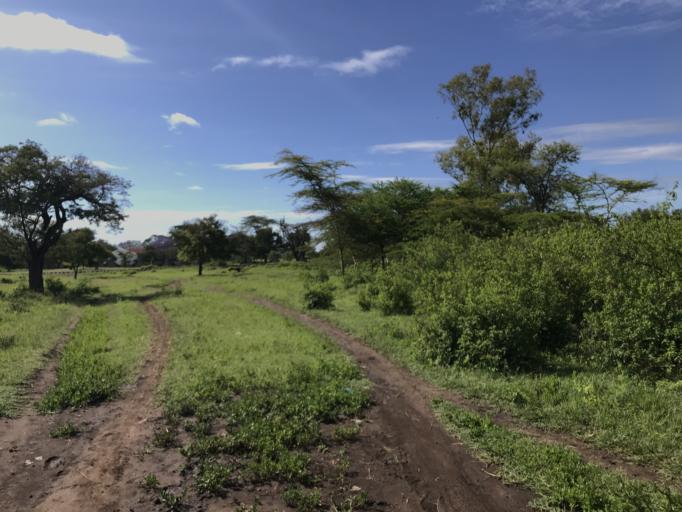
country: TZ
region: Arusha
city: Usa River
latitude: -3.3970
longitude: 36.7973
